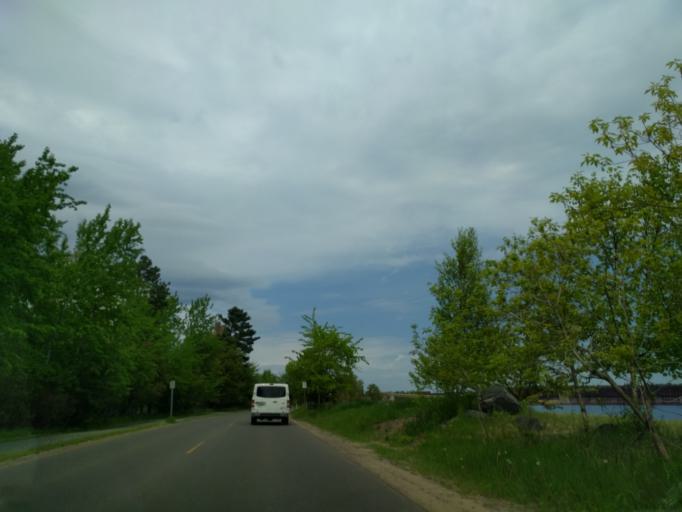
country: US
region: Michigan
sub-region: Marquette County
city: Marquette
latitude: 46.5719
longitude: -87.3934
